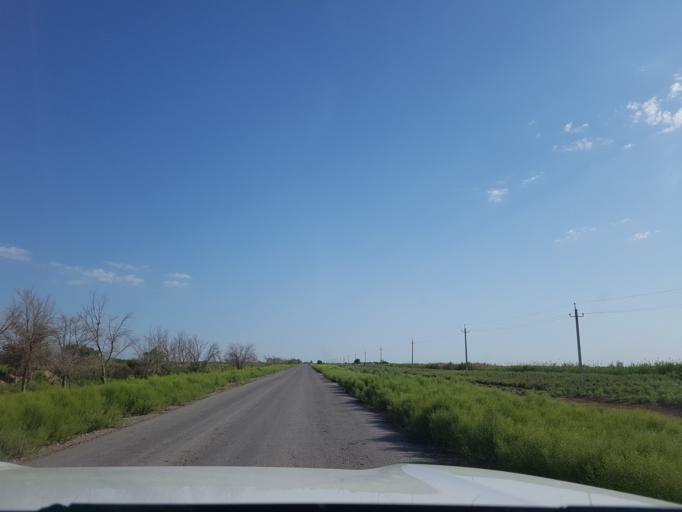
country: TM
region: Dasoguz
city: Koeneuergench
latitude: 41.8898
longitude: 58.7069
